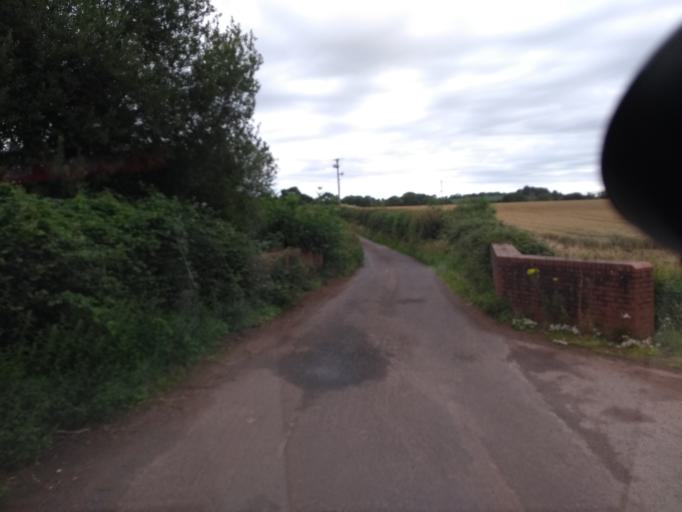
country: GB
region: England
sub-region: Somerset
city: Bridgwater
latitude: 51.1414
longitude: -3.0936
